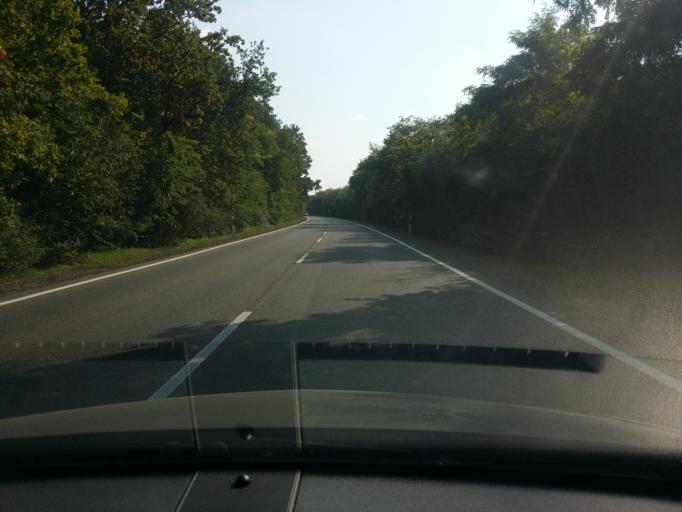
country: HU
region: Fejer
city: dunaujvaros
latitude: 46.9458
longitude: 18.9145
